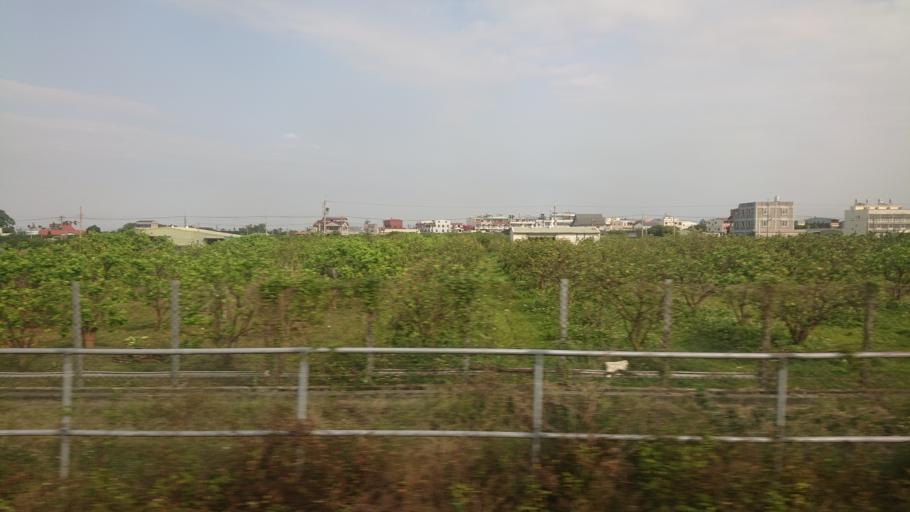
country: TW
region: Taiwan
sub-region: Yunlin
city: Douliu
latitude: 23.7149
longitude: 120.5561
